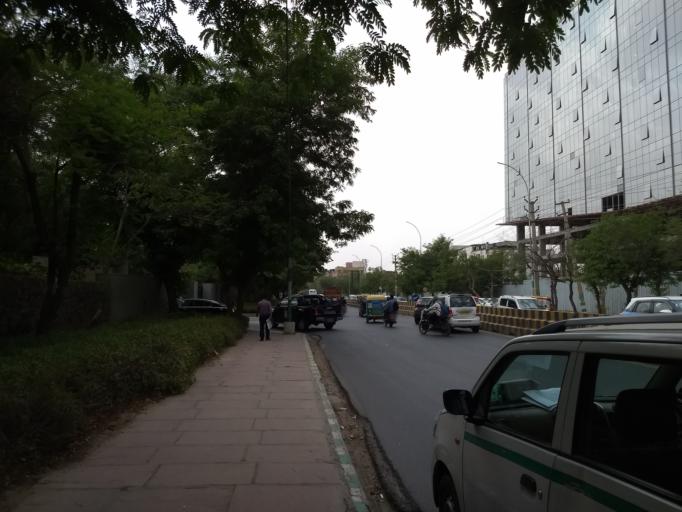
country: IN
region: Haryana
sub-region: Gurgaon
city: Gurgaon
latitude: 28.5027
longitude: 77.0891
